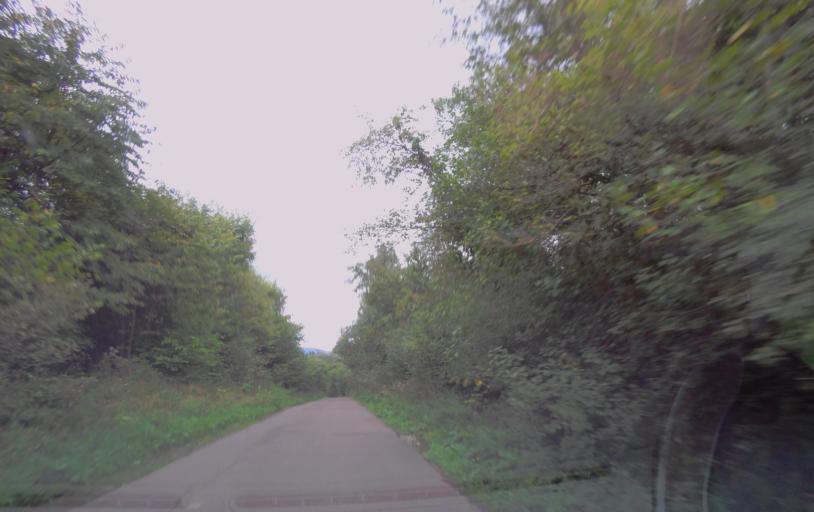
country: PL
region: Subcarpathian Voivodeship
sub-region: Powiat leski
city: Polanczyk
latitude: 49.3024
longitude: 22.5111
